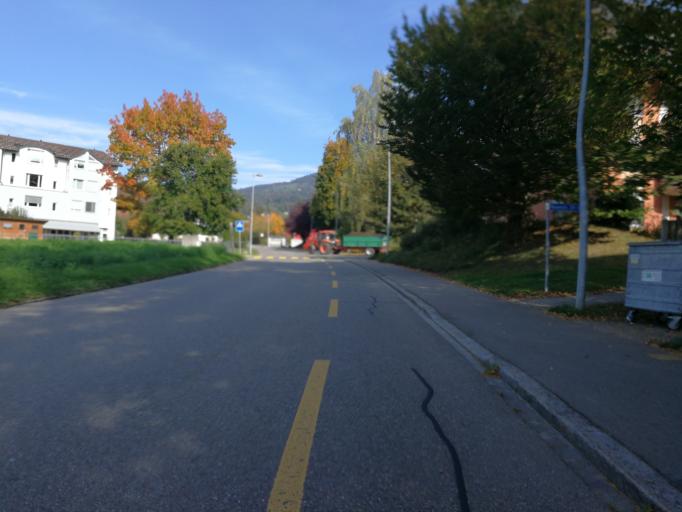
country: CH
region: Zurich
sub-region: Bezirk Hinwil
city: Tann
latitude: 47.2728
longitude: 8.8547
